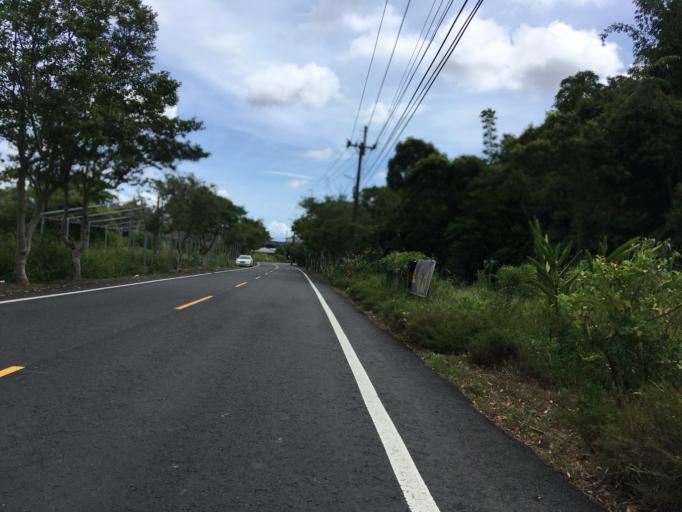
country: TW
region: Taiwan
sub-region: Yilan
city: Yilan
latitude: 24.6306
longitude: 121.7116
